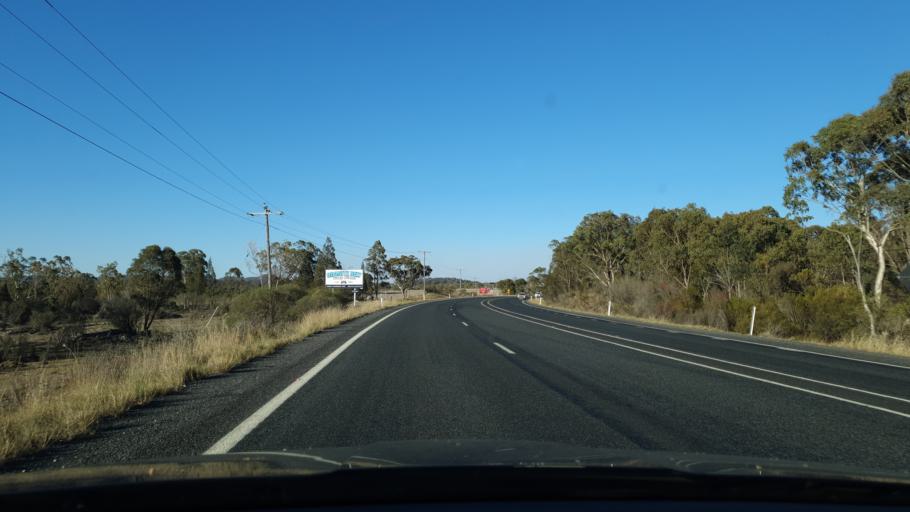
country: AU
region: Queensland
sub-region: Southern Downs
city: Stanthorpe
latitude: -28.6917
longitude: 151.9080
